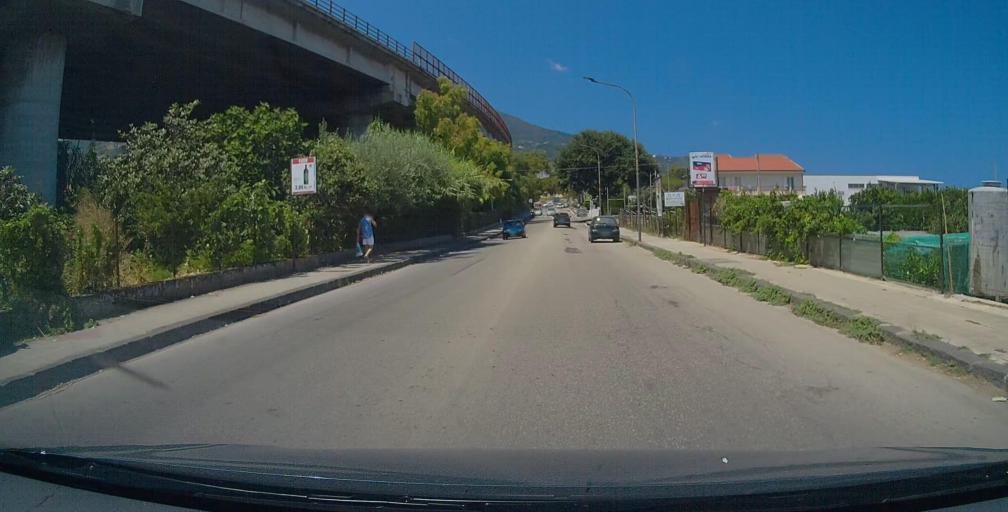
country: IT
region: Sicily
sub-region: Messina
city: Patti
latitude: 38.1493
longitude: 14.9743
